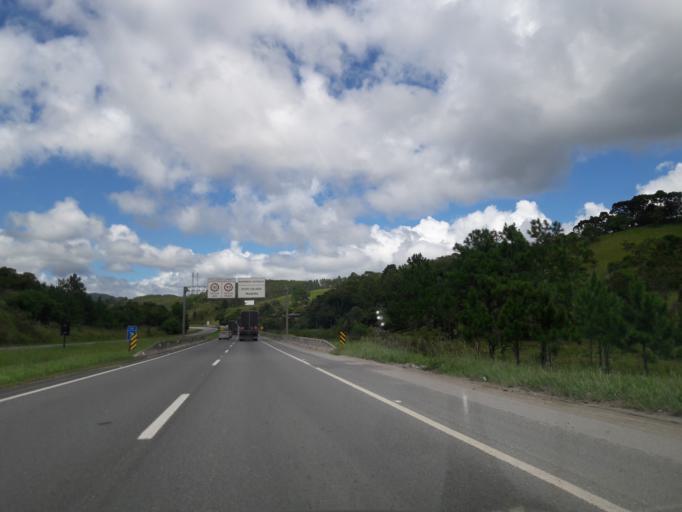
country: BR
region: Parana
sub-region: Campina Grande Do Sul
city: Campina Grande do Sul
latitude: -25.1233
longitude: -48.8563
